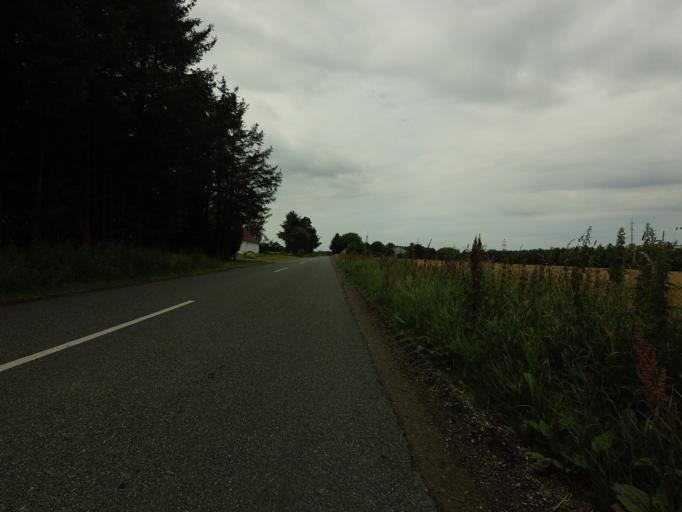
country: DK
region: North Denmark
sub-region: Alborg Kommune
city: Vadum
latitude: 57.1306
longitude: 9.8513
